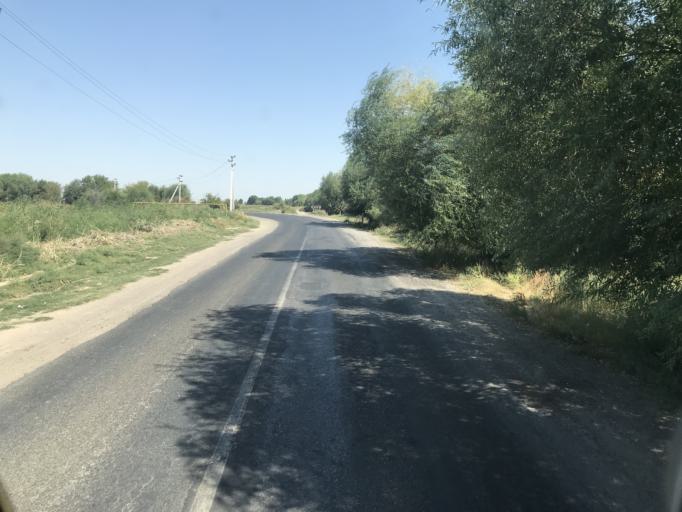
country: KZ
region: Ongtustik Qazaqstan
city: Ilyich
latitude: 40.9468
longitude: 68.4888
